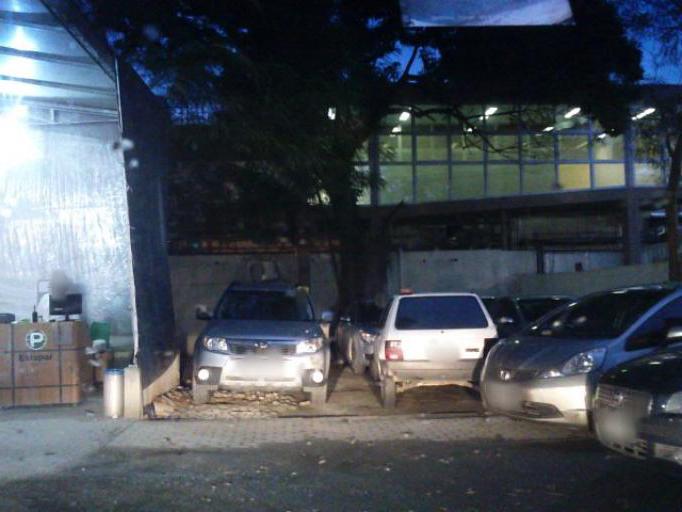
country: BR
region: Sao Paulo
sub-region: Sao Jose Dos Campos
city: Sao Jose dos Campos
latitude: -23.1984
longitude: -45.9167
